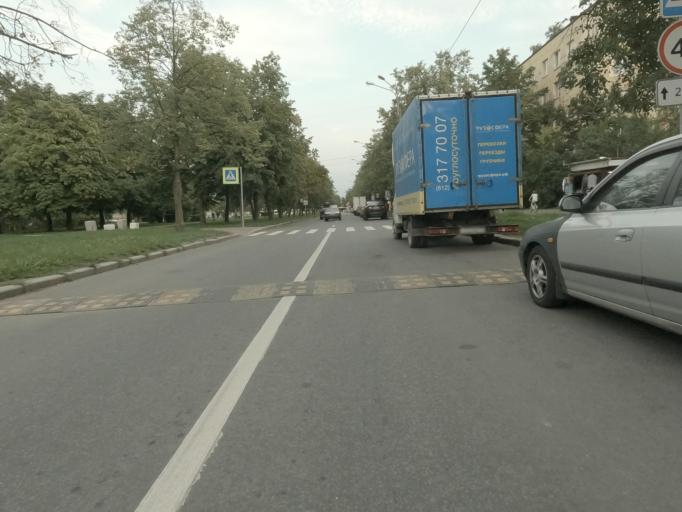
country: RU
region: St.-Petersburg
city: Dachnoye
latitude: 59.8451
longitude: 30.2719
